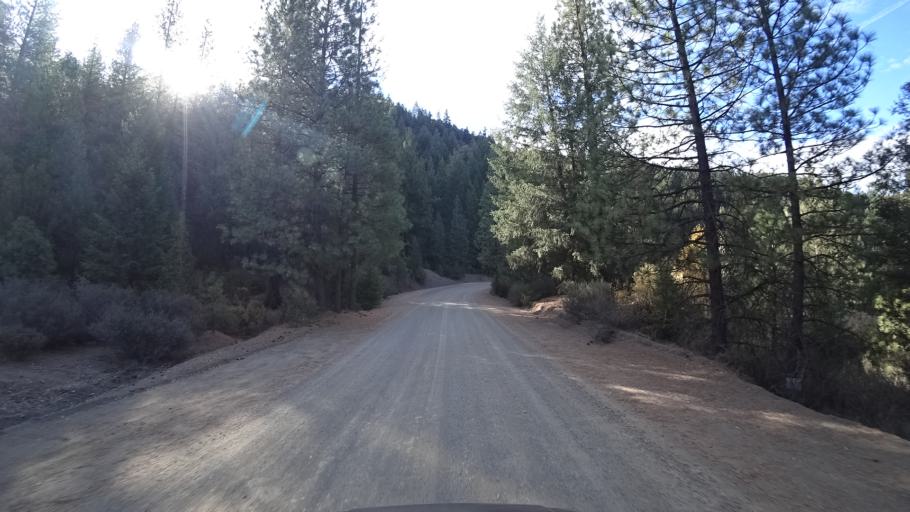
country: US
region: California
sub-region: Siskiyou County
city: Yreka
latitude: 41.7163
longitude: -122.7806
